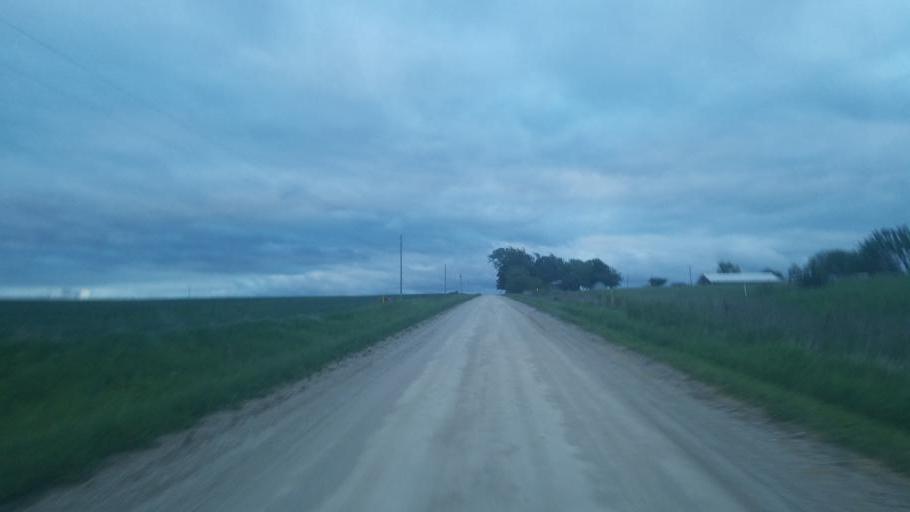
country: US
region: Iowa
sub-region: Decatur County
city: Lamoni
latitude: 40.5947
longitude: -93.9477
